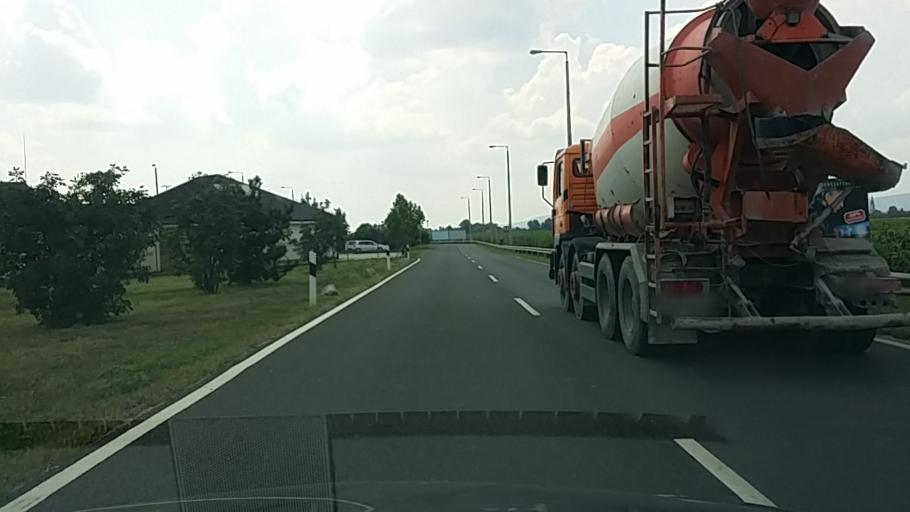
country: HU
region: Budapest
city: Budapest XV. keruelet
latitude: 47.5680
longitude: 19.1462
